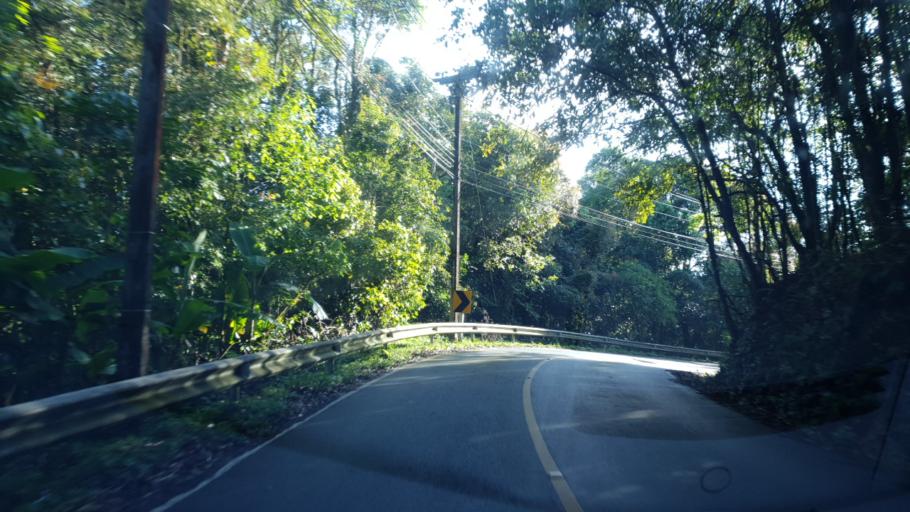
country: TH
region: Chiang Mai
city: Mae Chaem
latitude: 18.5251
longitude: 98.4927
